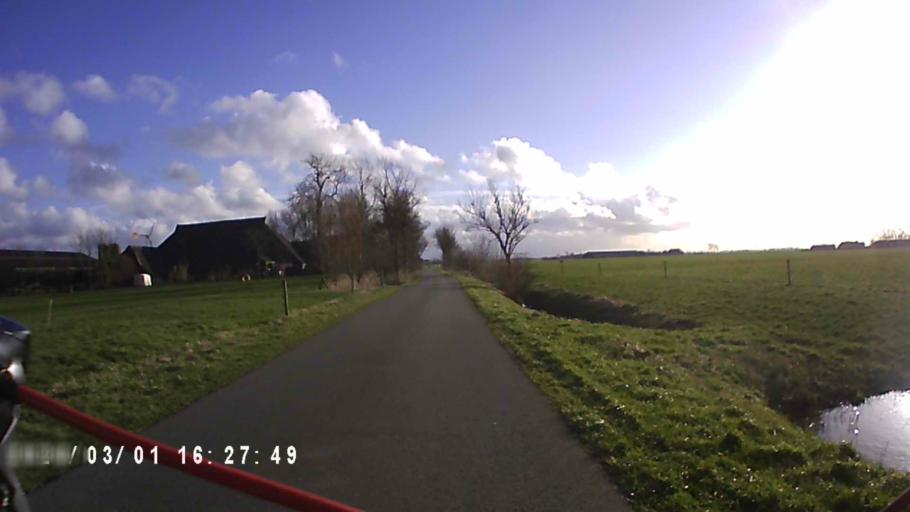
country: NL
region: Groningen
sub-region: Gemeente Zuidhorn
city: Oldehove
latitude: 53.3054
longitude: 6.4288
